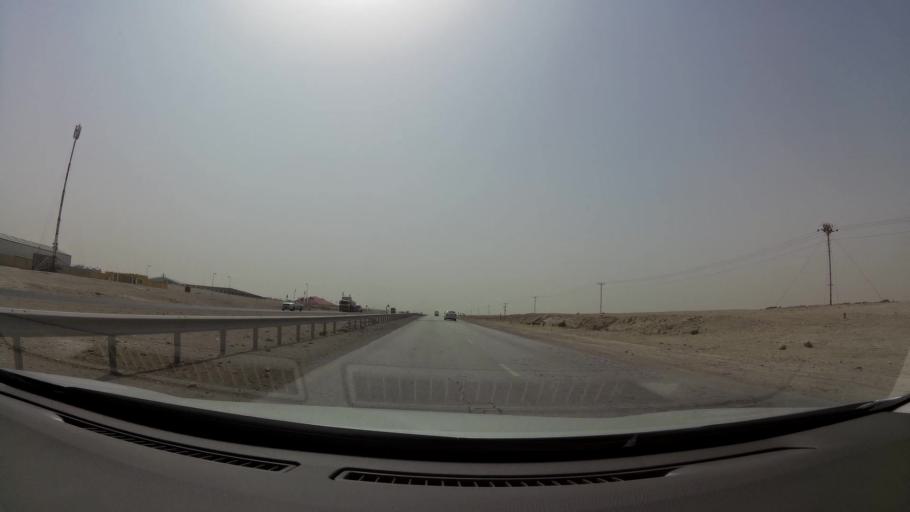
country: QA
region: Baladiyat ar Rayyan
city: Ar Rayyan
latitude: 25.2214
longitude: 51.3650
